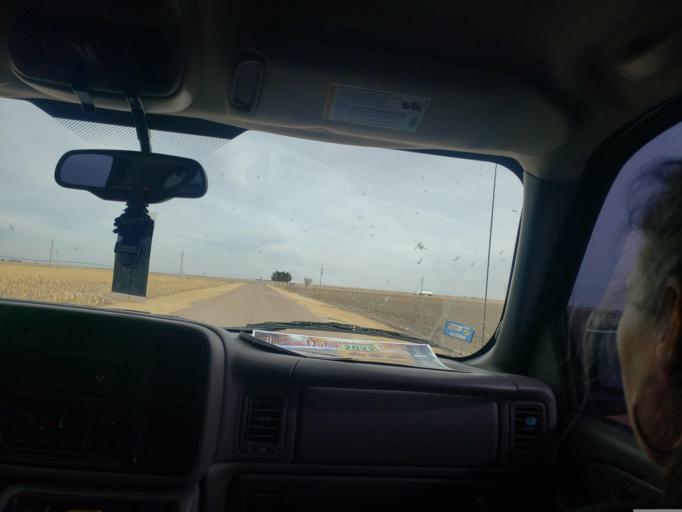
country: US
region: Kansas
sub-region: Finney County
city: Garden City
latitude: 37.9241
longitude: -100.7125
